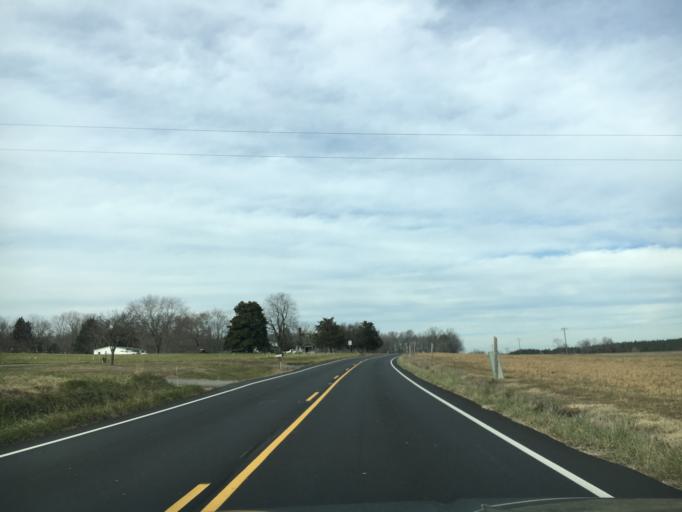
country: US
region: Virginia
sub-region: Goochland County
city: Goochland
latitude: 37.8119
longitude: -77.8688
